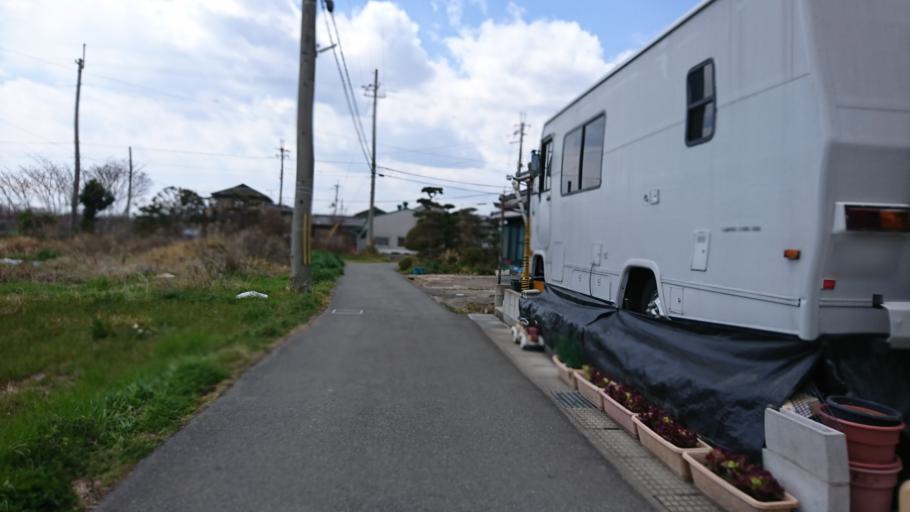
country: JP
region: Hyogo
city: Kakogawacho-honmachi
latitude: 34.7553
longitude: 134.9025
